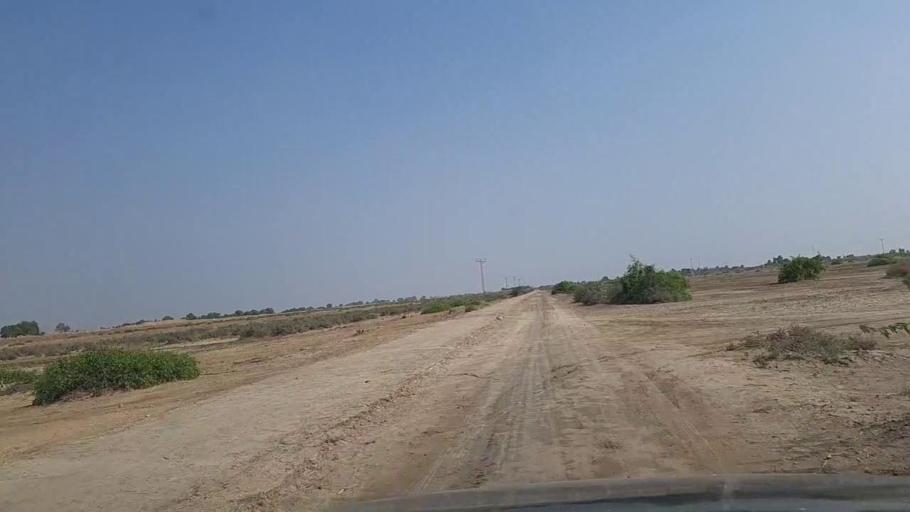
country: PK
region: Sindh
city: Gharo
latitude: 24.7413
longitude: 67.6470
